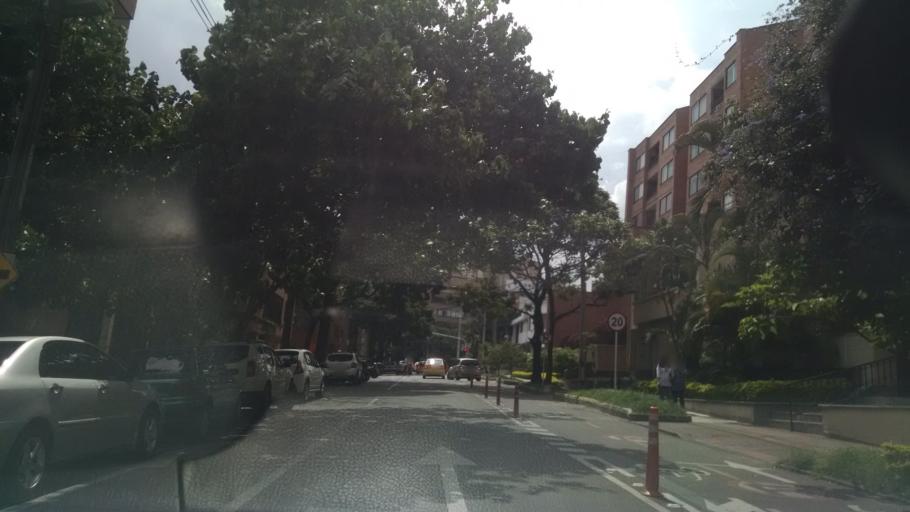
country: CO
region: Antioquia
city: Medellin
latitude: 6.2415
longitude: -75.5959
